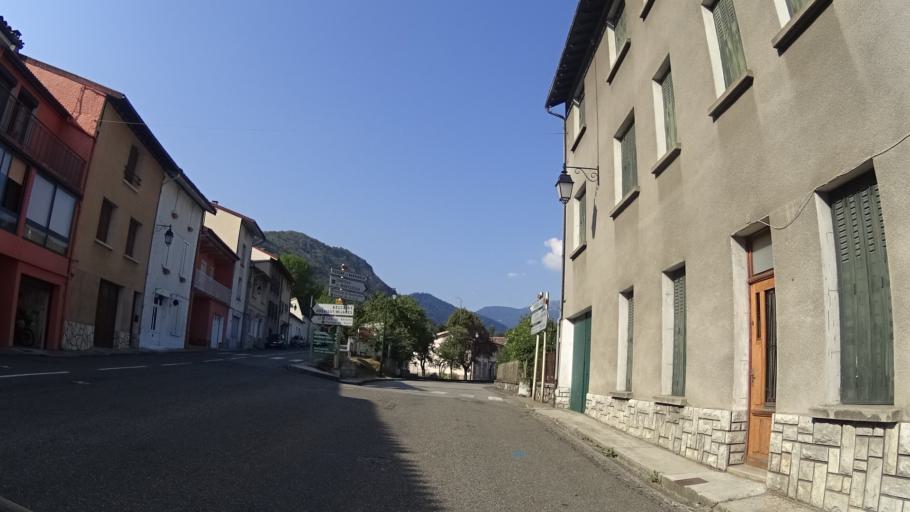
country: FR
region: Midi-Pyrenees
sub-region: Departement de l'Ariege
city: Belesta
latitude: 42.9015
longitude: 1.9346
